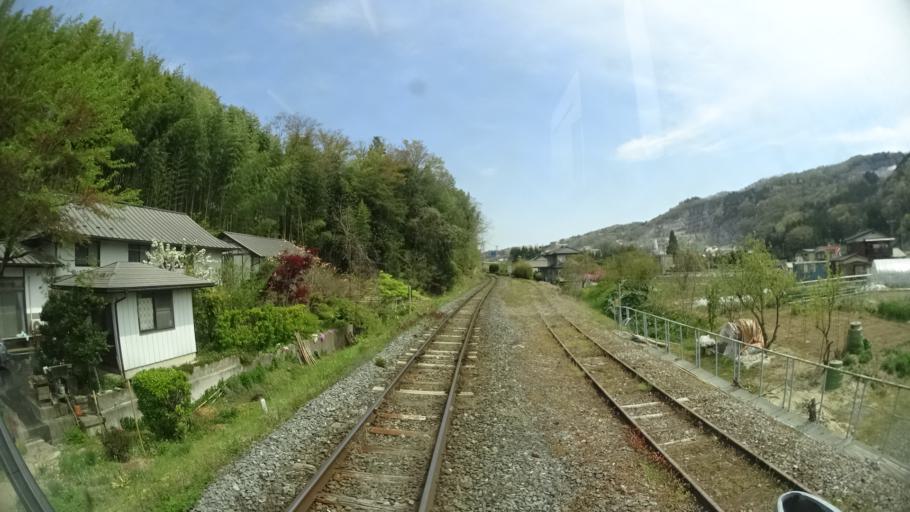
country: JP
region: Iwate
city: Ichinoseki
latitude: 38.9806
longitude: 141.2401
